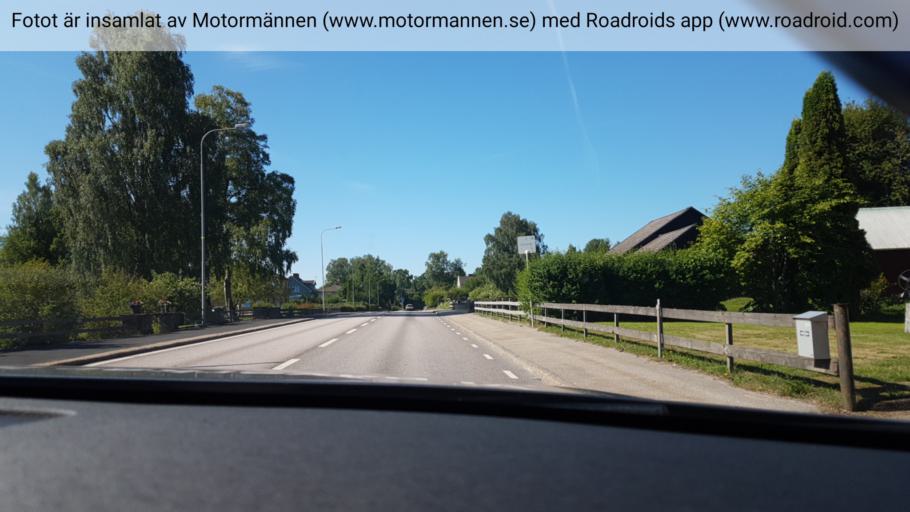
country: SE
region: Vaestra Goetaland
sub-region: Ulricehamns Kommun
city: Ulricehamn
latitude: 57.9039
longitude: 13.4722
